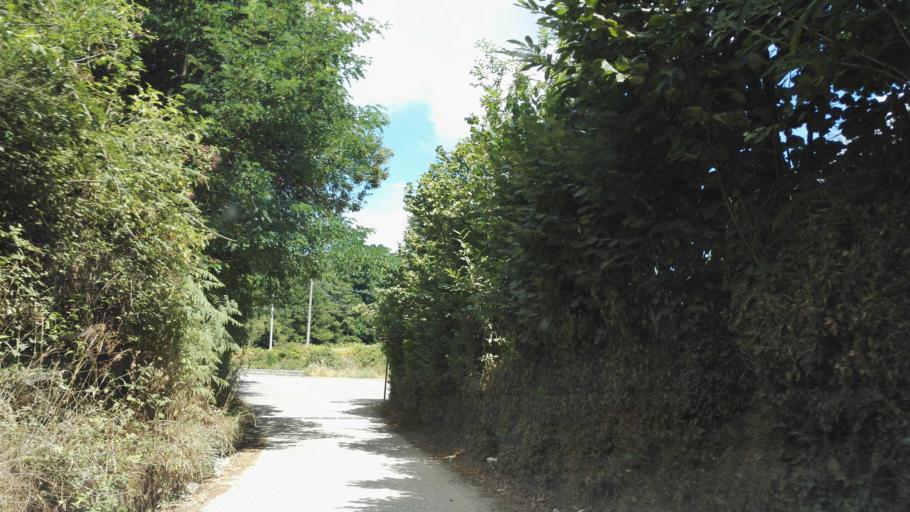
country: IT
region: Calabria
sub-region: Provincia di Vibo-Valentia
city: Serra San Bruno
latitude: 38.5642
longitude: 16.3295
